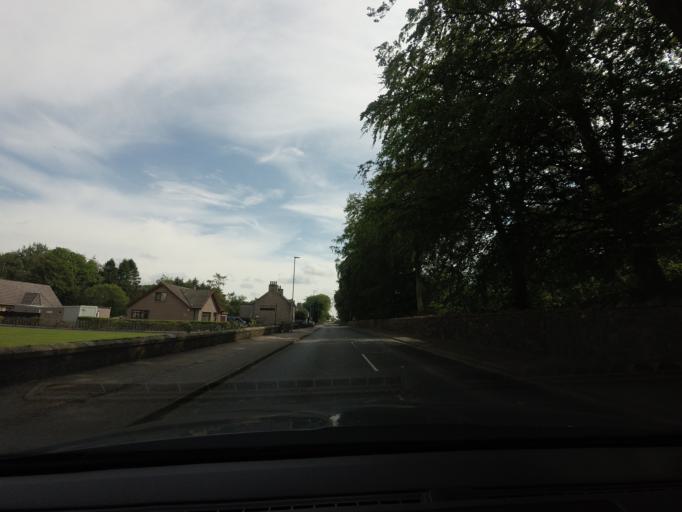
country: GB
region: Scotland
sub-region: Aberdeenshire
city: Mintlaw
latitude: 57.5260
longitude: -2.0230
